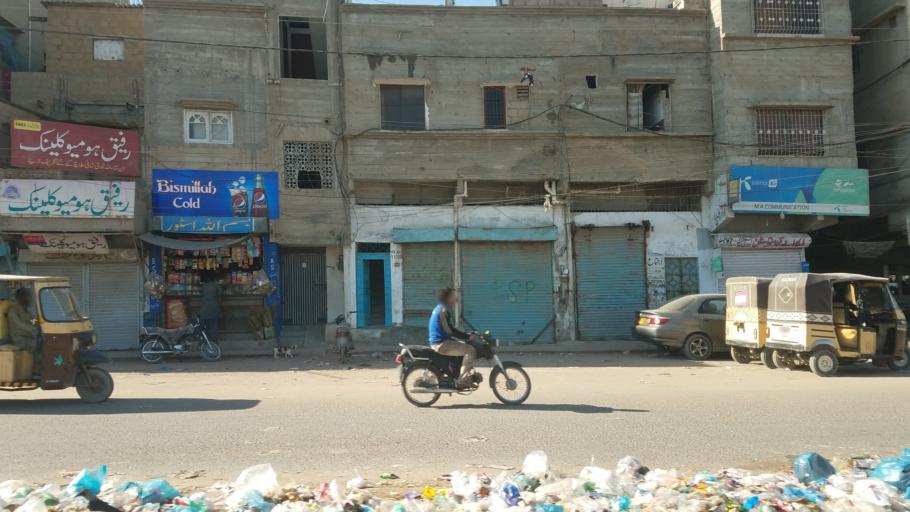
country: PK
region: Sindh
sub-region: Karachi District
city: Karachi
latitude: 24.9219
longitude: 67.0499
